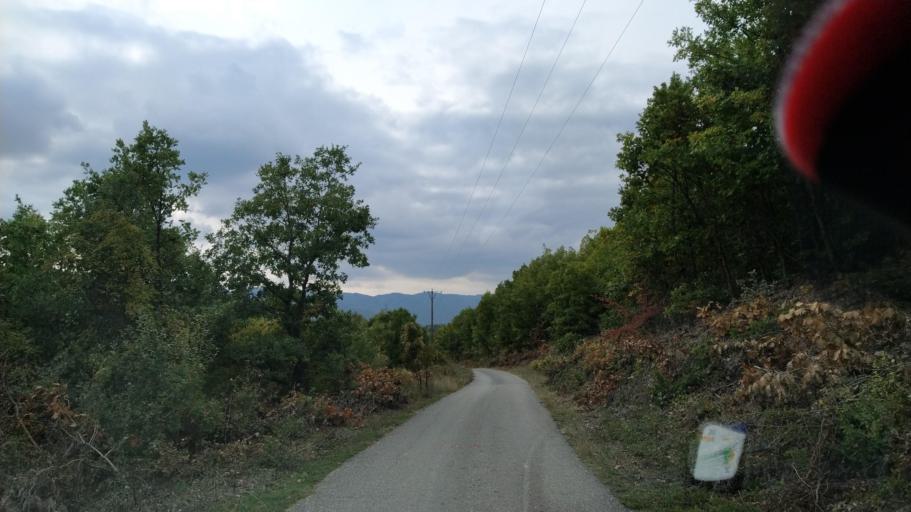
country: MK
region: Konce
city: Konce
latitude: 41.5076
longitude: 22.4749
